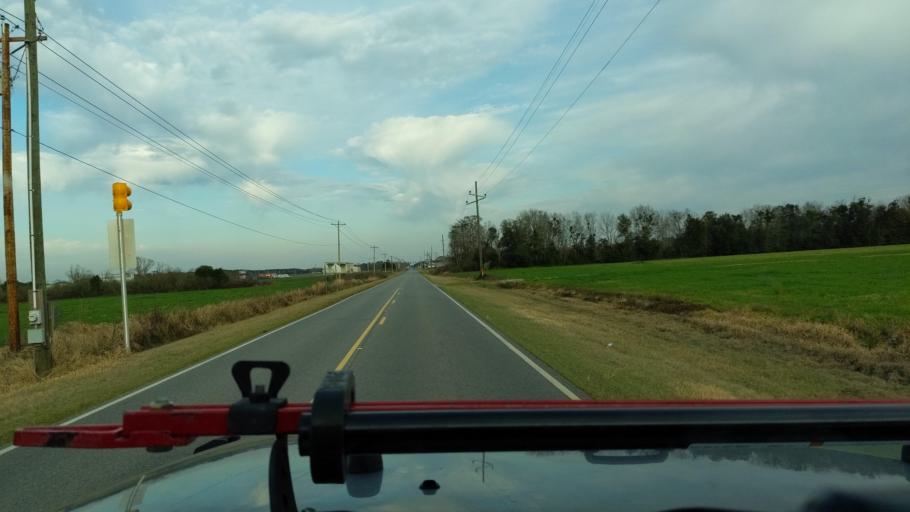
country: US
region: Alabama
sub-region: Baldwin County
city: Foley
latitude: 30.4581
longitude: -87.6982
